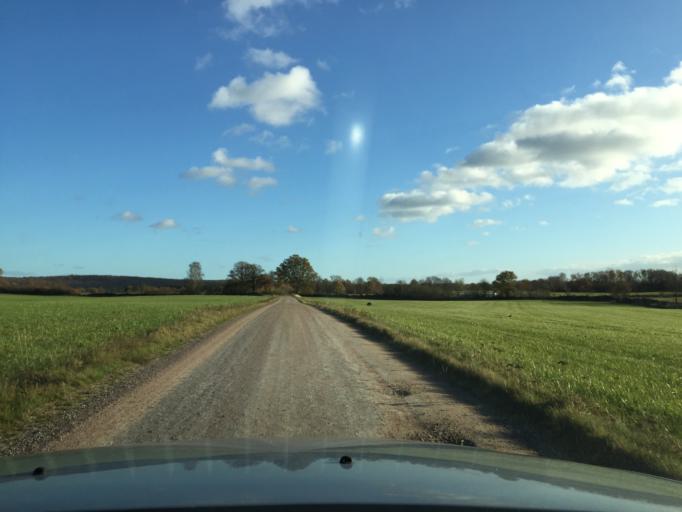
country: SE
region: Skane
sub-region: Hassleholms Kommun
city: Tormestorp
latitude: 56.0675
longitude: 13.7150
